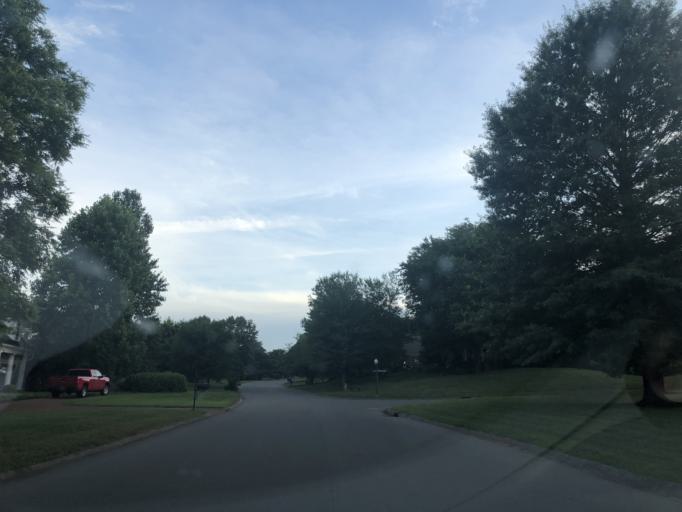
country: US
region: Tennessee
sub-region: Davidson County
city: Forest Hills
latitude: 36.0460
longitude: -86.9264
